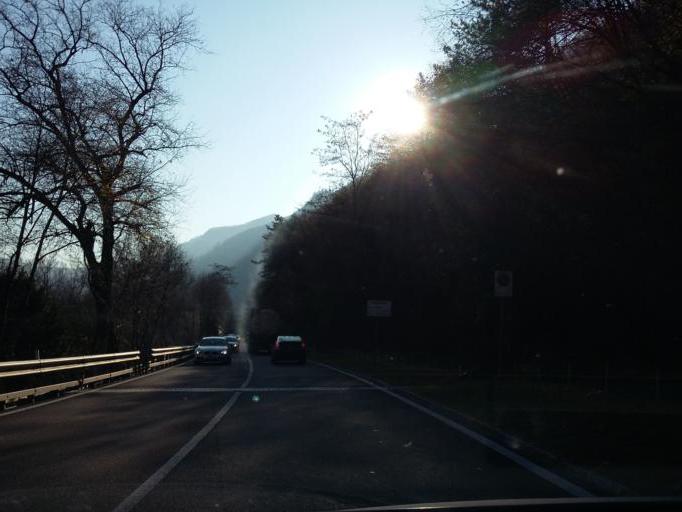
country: IT
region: Trentino-Alto Adige
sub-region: Provincia di Trento
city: Nago-Torbole
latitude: 45.8617
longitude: 10.9173
